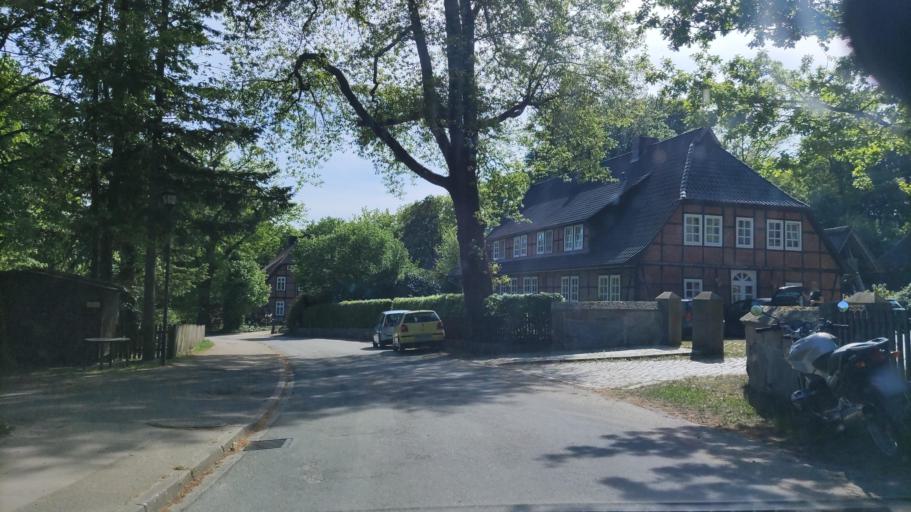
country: DE
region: Lower Saxony
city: Undeloh
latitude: 53.1457
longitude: 9.9221
